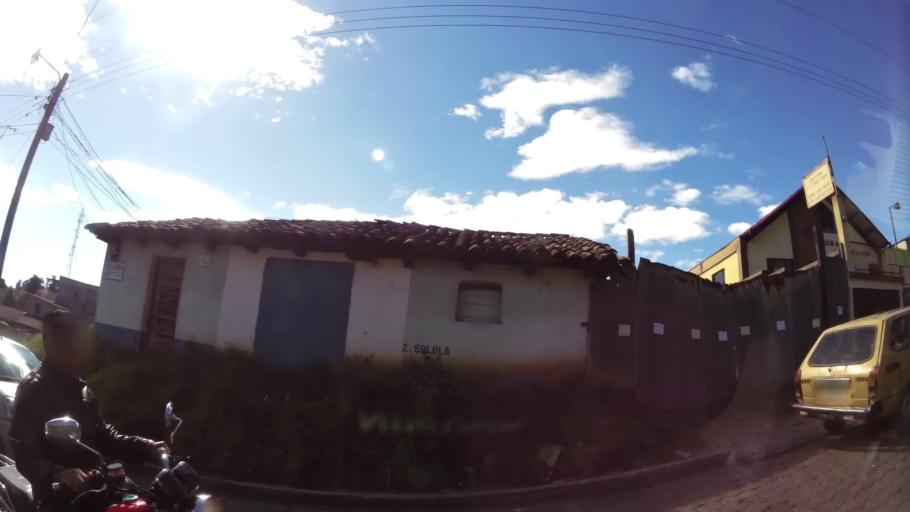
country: GT
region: Solola
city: Solola
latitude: 14.7774
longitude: -91.1830
